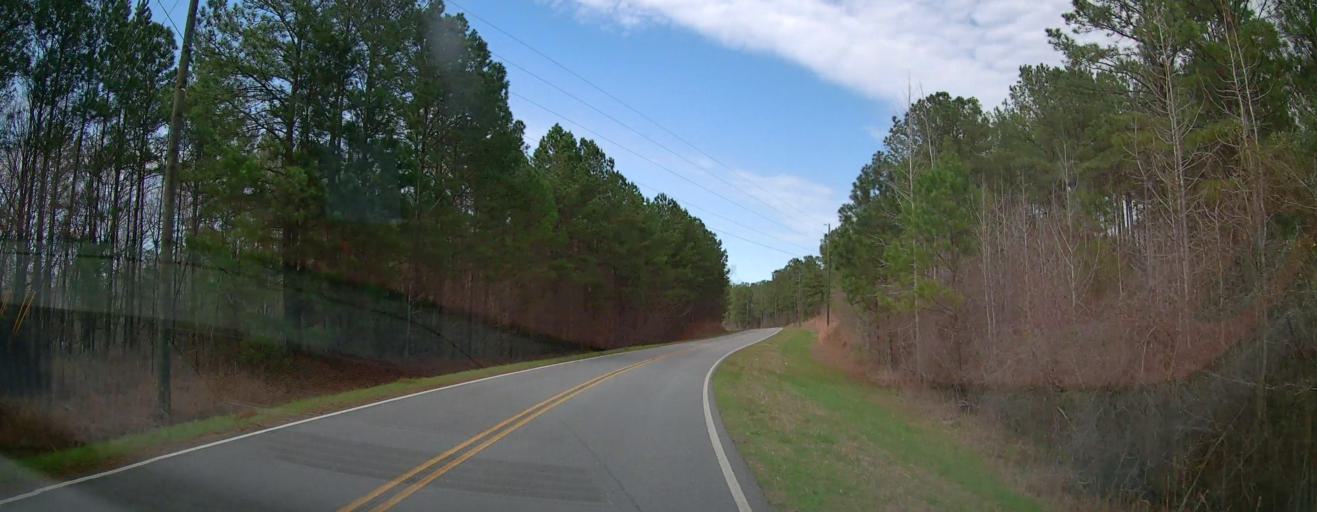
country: US
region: Georgia
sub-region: Jones County
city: Gray
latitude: 33.0563
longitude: -83.7242
